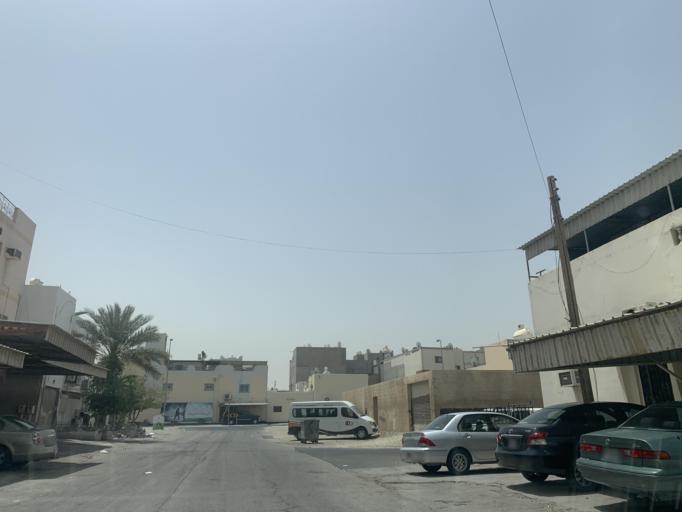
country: BH
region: Northern
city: Madinat `Isa
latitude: 26.1527
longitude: 50.5213
